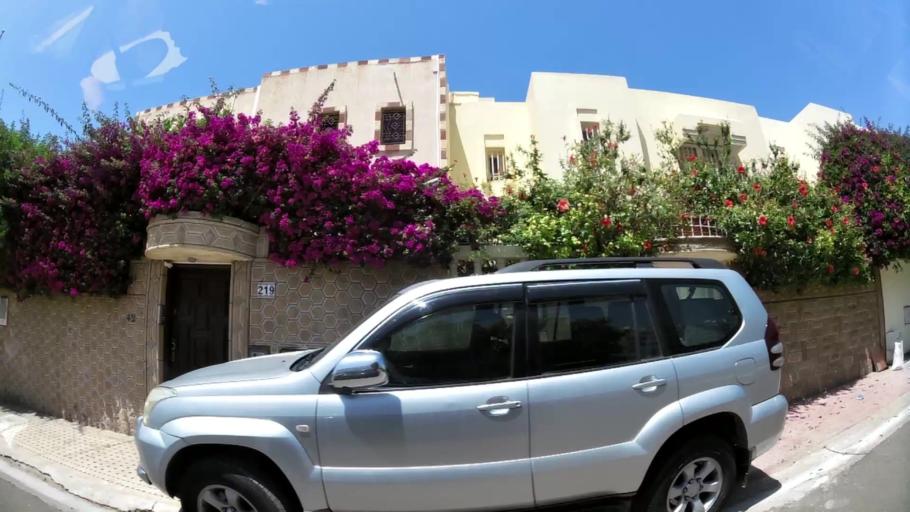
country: MA
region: Souss-Massa-Draa
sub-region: Agadir-Ida-ou-Tnan
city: Agadir
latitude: 30.4347
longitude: -9.5811
